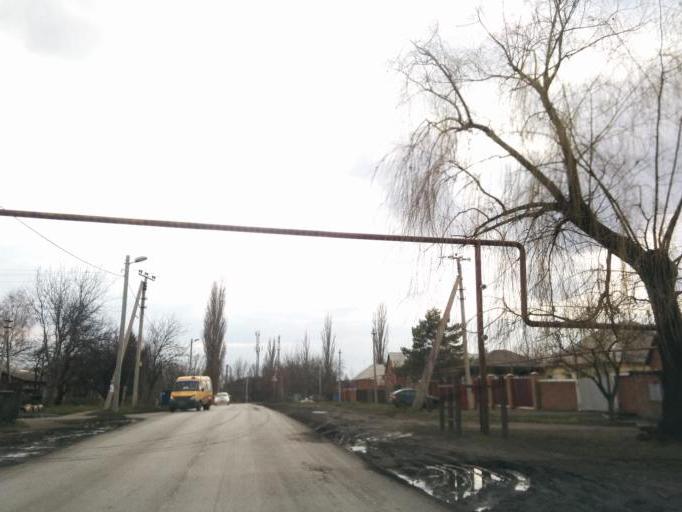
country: RU
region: Rostov
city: Shakhty
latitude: 47.6843
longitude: 40.2860
